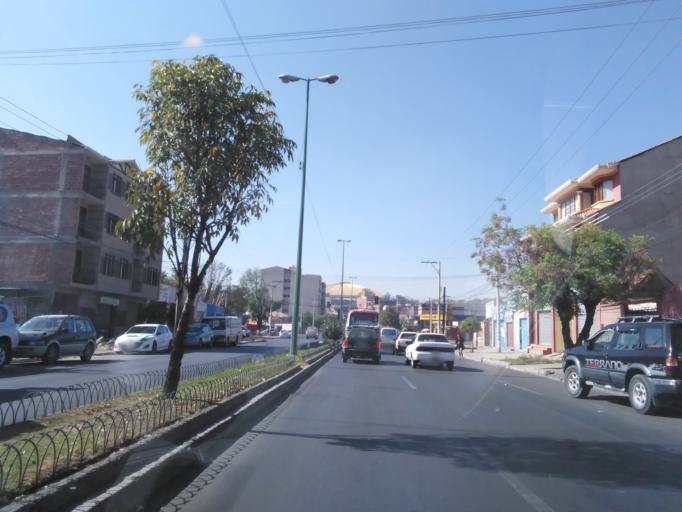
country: BO
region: Cochabamba
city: Cochabamba
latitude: -17.3977
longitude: -66.1665
